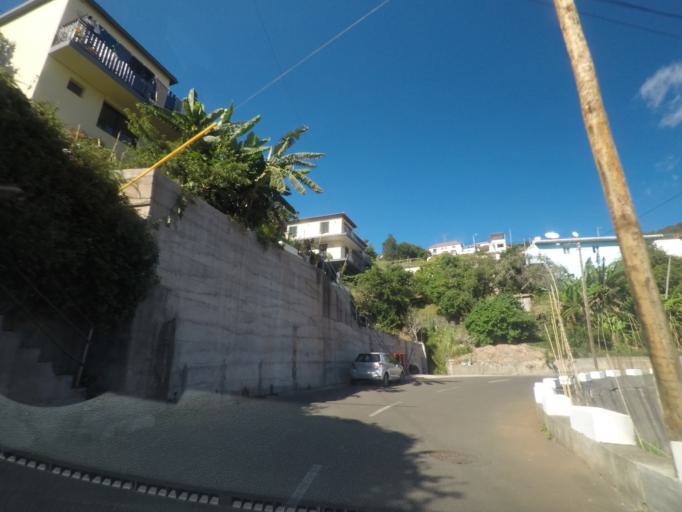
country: PT
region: Madeira
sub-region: Ribeira Brava
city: Campanario
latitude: 32.6774
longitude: -17.0255
